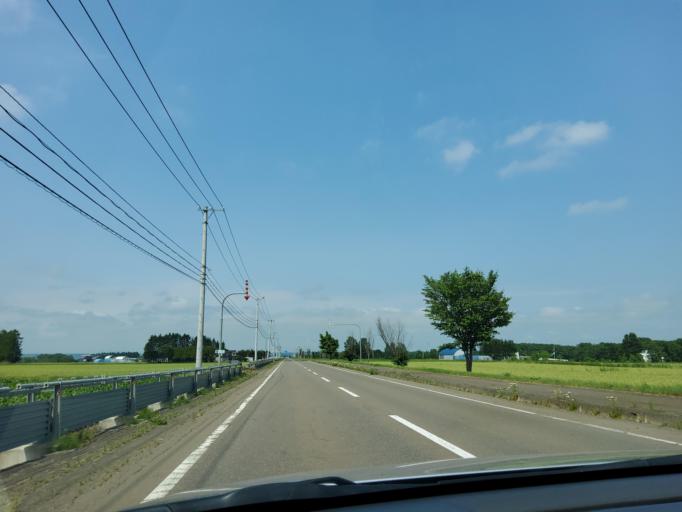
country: JP
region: Hokkaido
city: Obihiro
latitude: 42.8866
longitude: 143.0361
